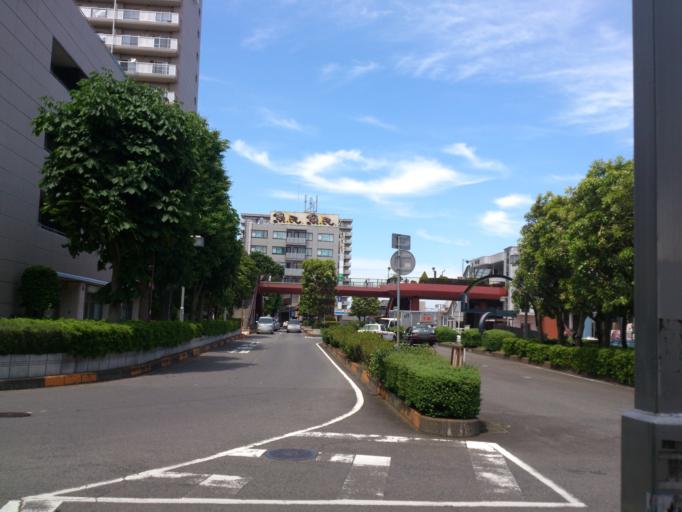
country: JP
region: Ibaraki
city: Ushiku
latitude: 35.9749
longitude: 140.1403
